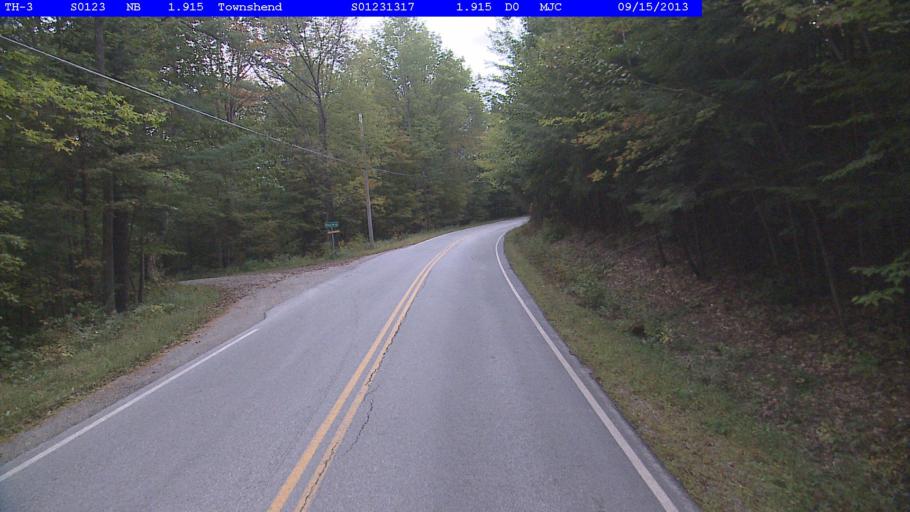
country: US
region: Vermont
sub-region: Windham County
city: Newfane
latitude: 43.1101
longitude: -72.7099
